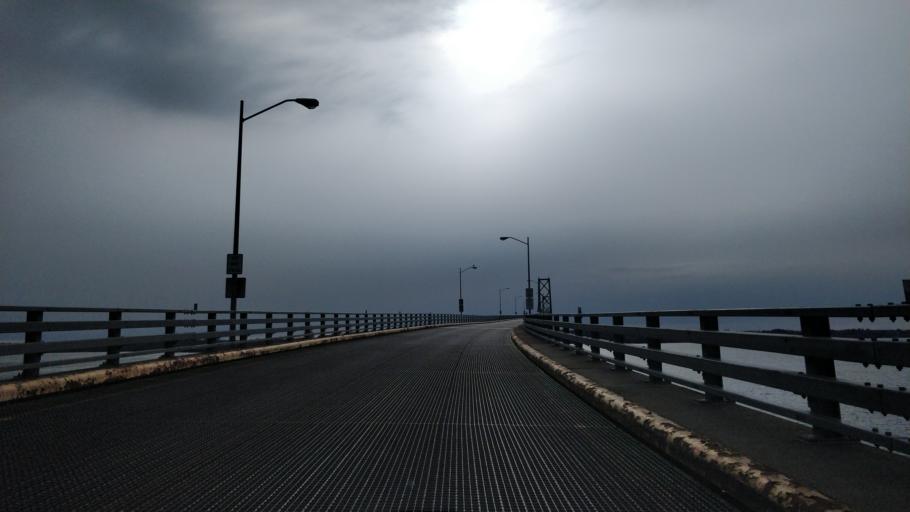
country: US
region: New York
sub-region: St. Lawrence County
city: Ogdensburg
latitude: 44.7429
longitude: -75.4655
